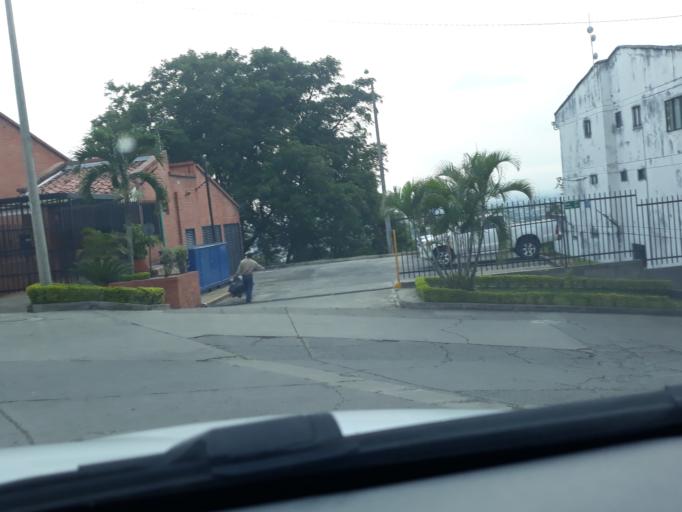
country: CO
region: Valle del Cauca
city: Cali
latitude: 3.4299
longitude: -76.5487
